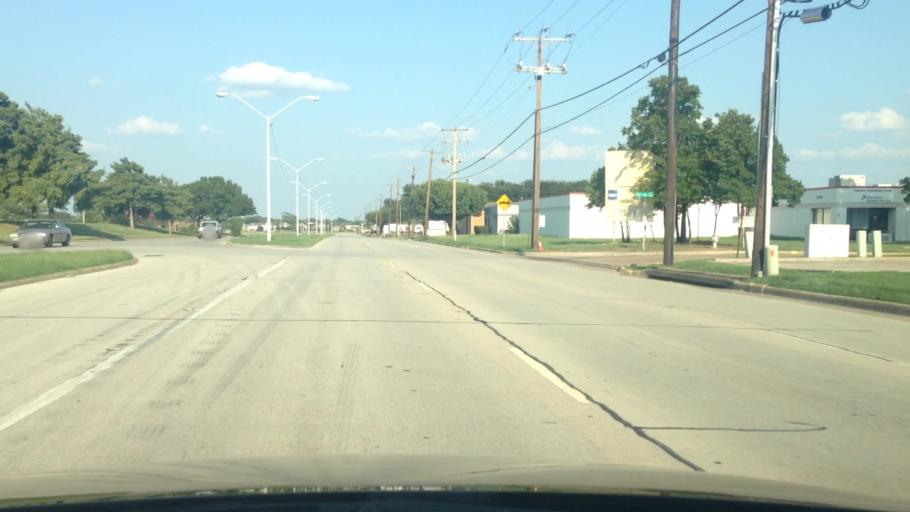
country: US
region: Texas
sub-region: Tarrant County
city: Everman
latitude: 32.6274
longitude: -97.3117
